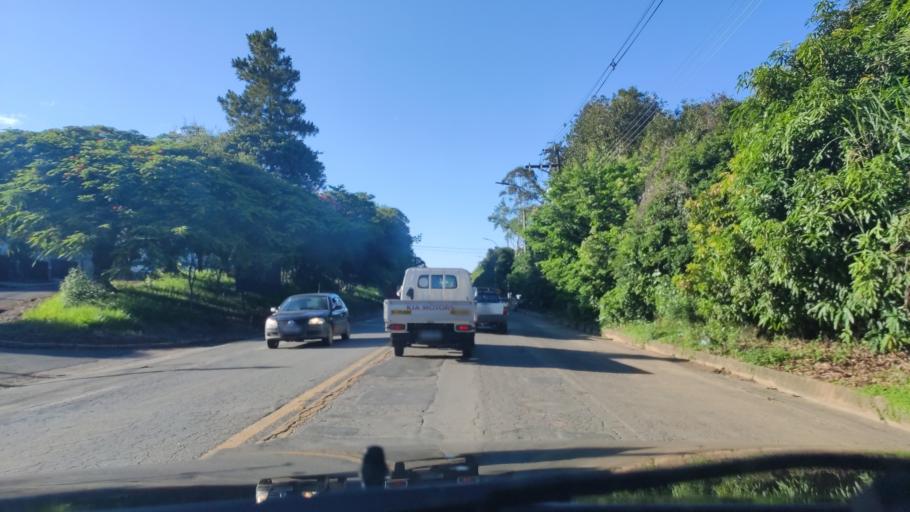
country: BR
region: Sao Paulo
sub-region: Socorro
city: Socorro
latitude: -22.5881
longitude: -46.5162
